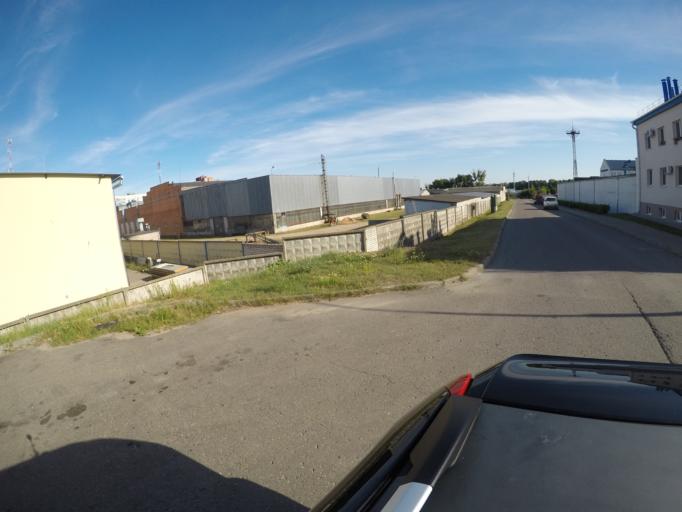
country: BY
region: Grodnenskaya
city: Hrodna
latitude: 53.7120
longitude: 23.8363
